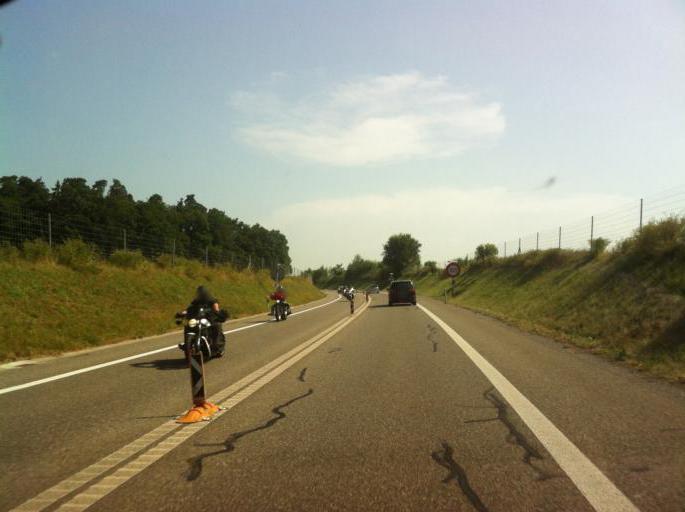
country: CH
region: Zurich
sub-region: Bezirk Andelfingen
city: Henggart
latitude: 47.5690
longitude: 8.6880
